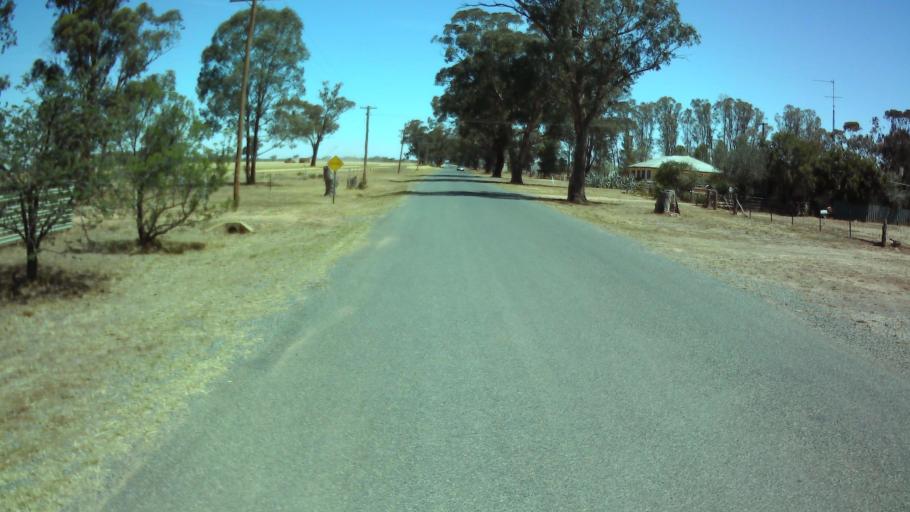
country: AU
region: New South Wales
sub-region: Weddin
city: Grenfell
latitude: -34.0137
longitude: 147.7941
